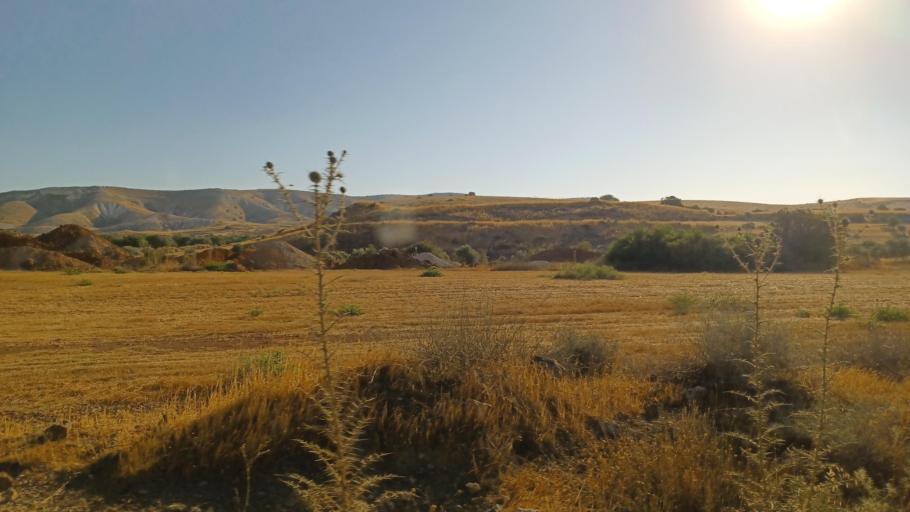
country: CY
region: Larnaka
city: Troulloi
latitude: 35.0307
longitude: 33.6263
